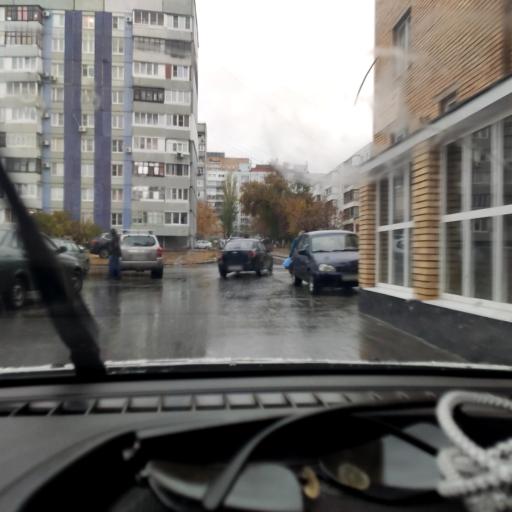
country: RU
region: Samara
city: Zhigulevsk
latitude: 53.4800
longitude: 49.4776
